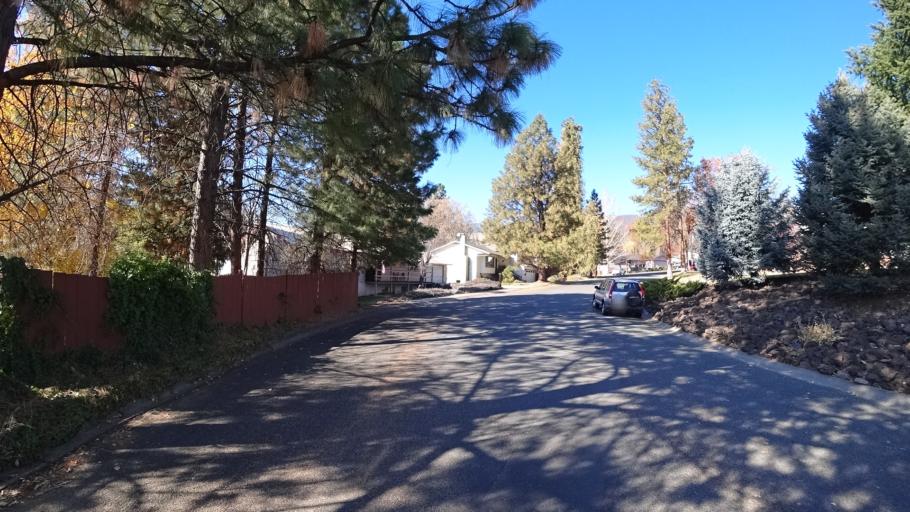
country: US
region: California
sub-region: Siskiyou County
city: Yreka
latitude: 41.7374
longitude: -122.6449
